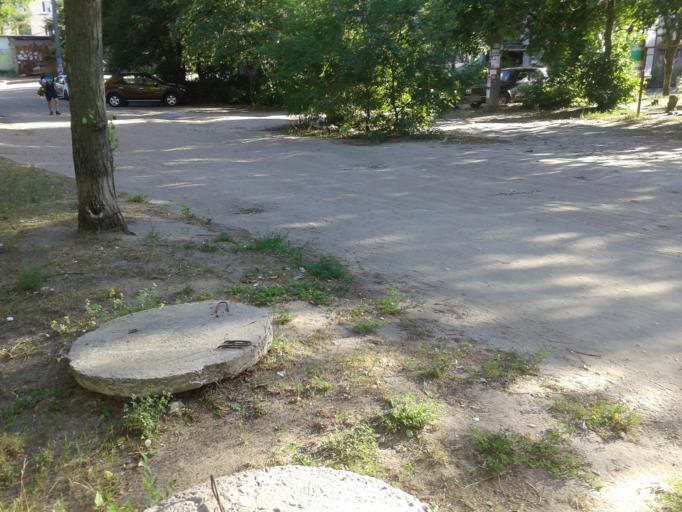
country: RU
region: Voronezj
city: Pridonskoy
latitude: 51.6552
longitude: 39.1229
